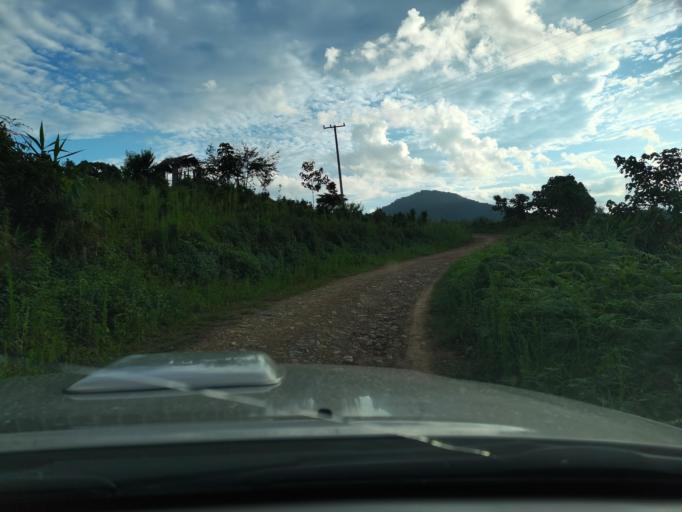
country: LA
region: Phongsali
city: Phongsali
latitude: 21.6695
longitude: 102.1832
